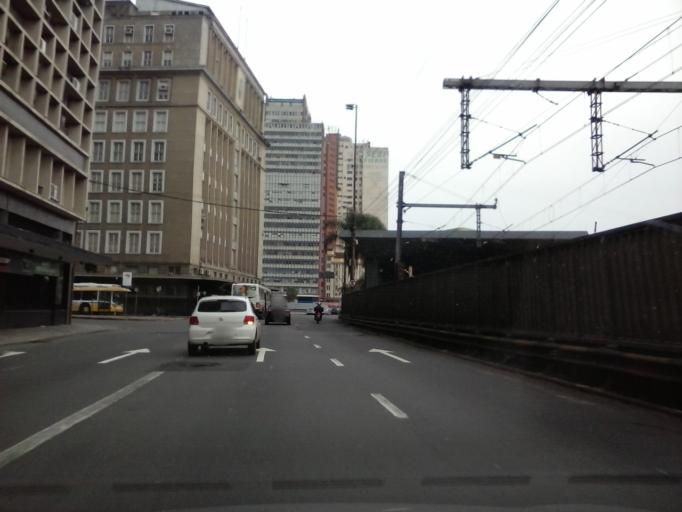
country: BR
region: Rio Grande do Sul
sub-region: Porto Alegre
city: Porto Alegre
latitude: -30.0259
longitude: -51.2267
